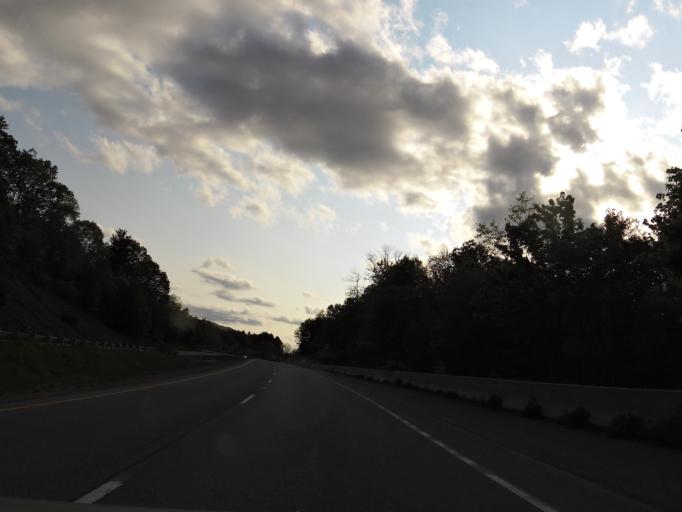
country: US
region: Virginia
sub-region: Tazewell County
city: Bluefield
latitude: 37.2403
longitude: -81.2733
